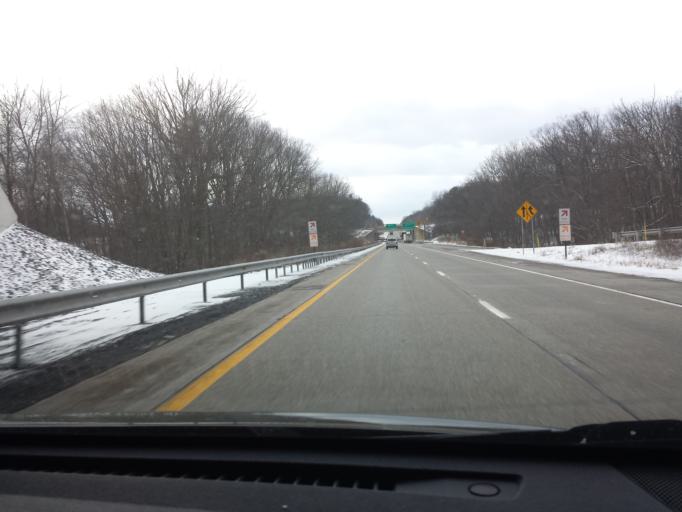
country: US
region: Pennsylvania
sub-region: Luzerne County
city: Conyngham
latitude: 41.0478
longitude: -76.0093
